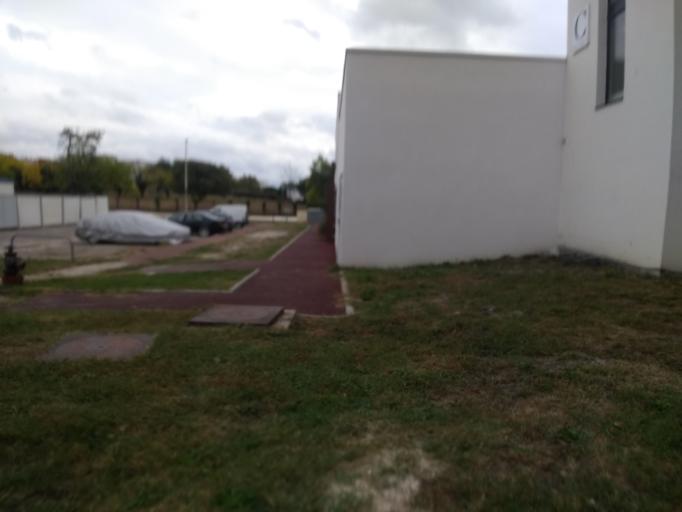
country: FR
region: Aquitaine
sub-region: Departement de la Gironde
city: Talence
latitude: 44.7944
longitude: -0.6130
